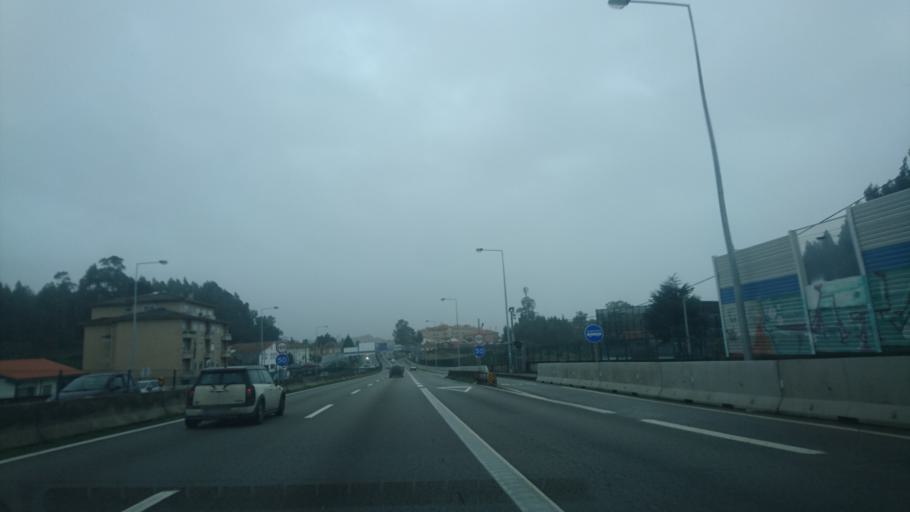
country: PT
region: Porto
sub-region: Vila Nova de Gaia
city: Vilar do Paraiso
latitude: 41.1058
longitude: -8.6265
